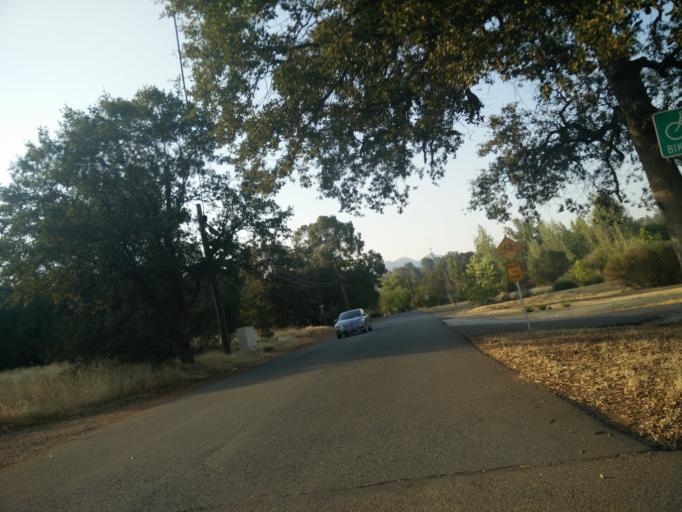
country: US
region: California
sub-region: Shasta County
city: Shasta Lake
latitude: 40.6805
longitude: -122.3522
